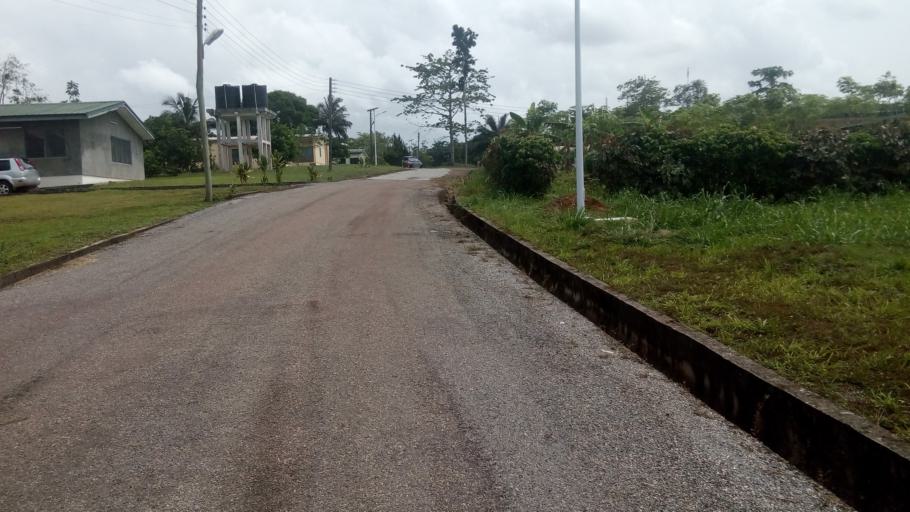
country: GH
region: Western
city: Tarkwa
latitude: 5.2966
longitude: -2.0127
